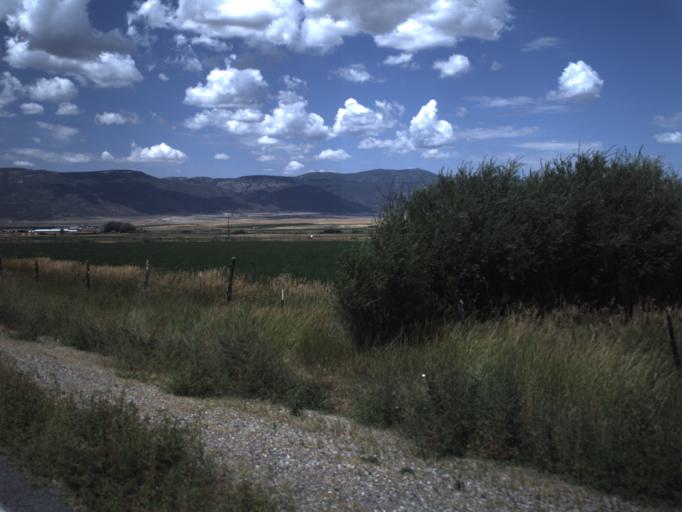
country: US
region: Utah
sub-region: Sanpete County
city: Moroni
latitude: 39.4811
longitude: -111.5182
